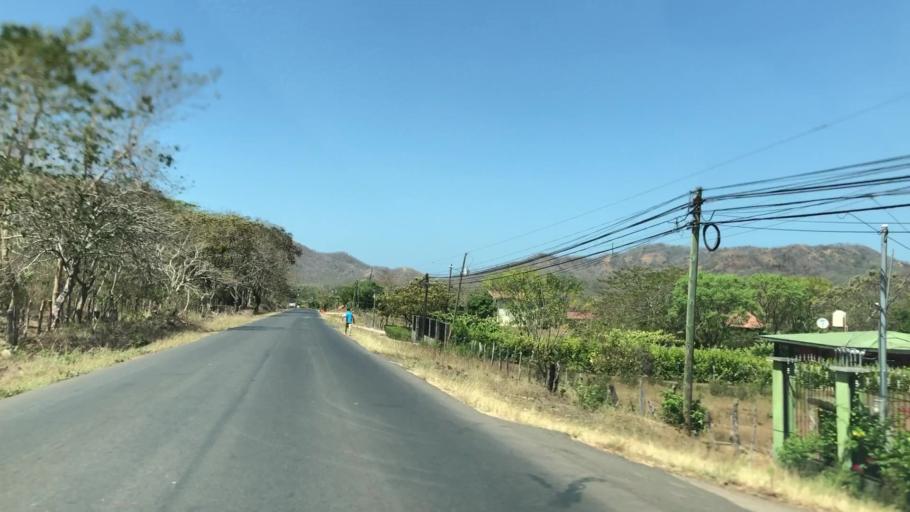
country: CR
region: Guanacaste
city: Sardinal
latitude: 10.3656
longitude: -85.8015
